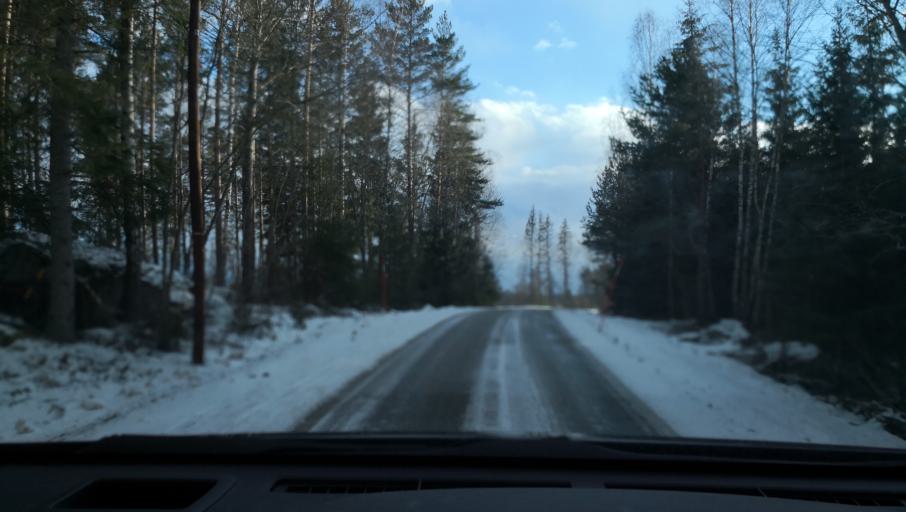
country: SE
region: Uppsala
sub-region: Enkopings Kommun
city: Irsta
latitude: 59.7002
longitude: 16.8678
